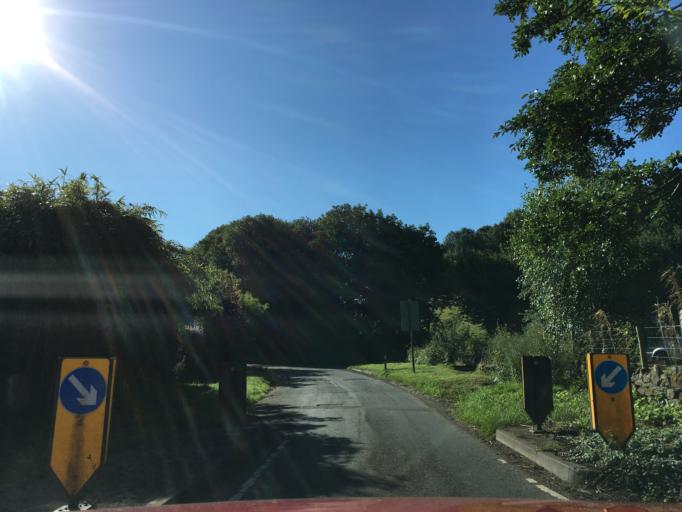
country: GB
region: England
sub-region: Gloucestershire
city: Coleford
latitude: 51.7806
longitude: -2.6448
